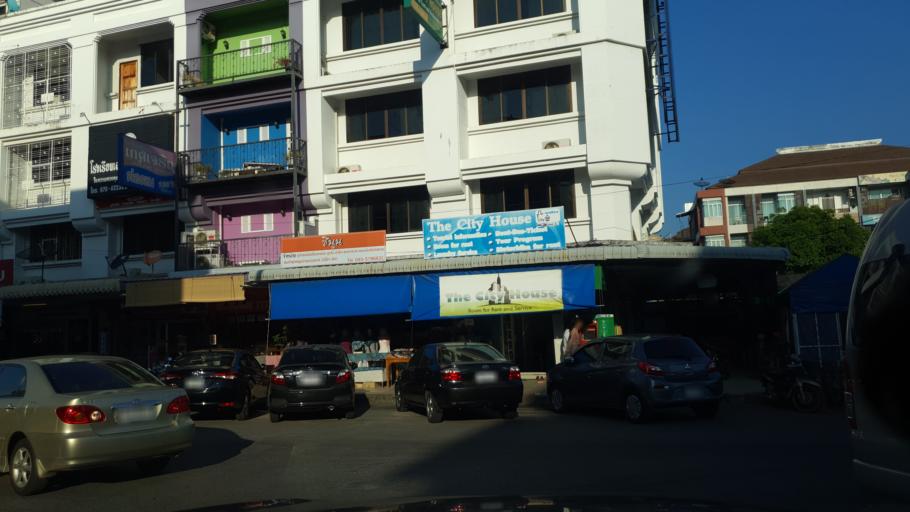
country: TH
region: Krabi
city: Krabi
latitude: 8.0657
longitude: 98.9159
